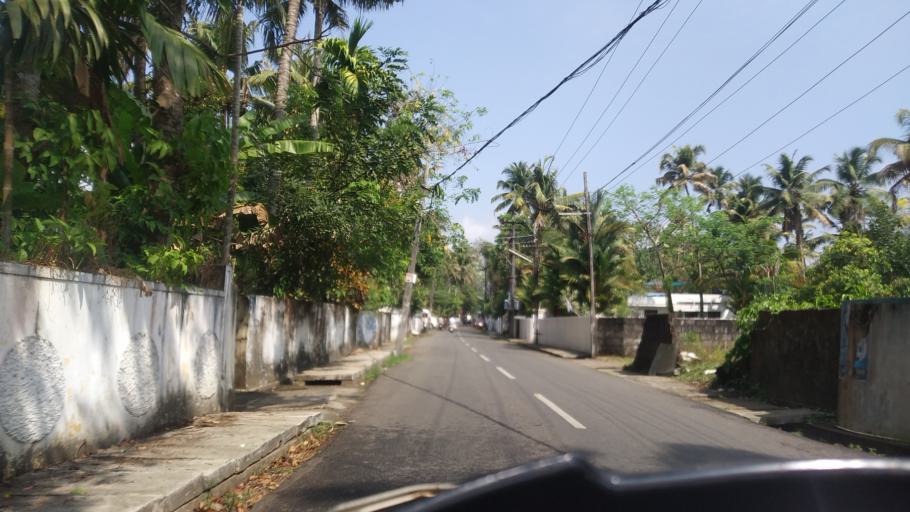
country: IN
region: Kerala
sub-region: Ernakulam
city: Elur
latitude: 10.1336
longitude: 76.2213
